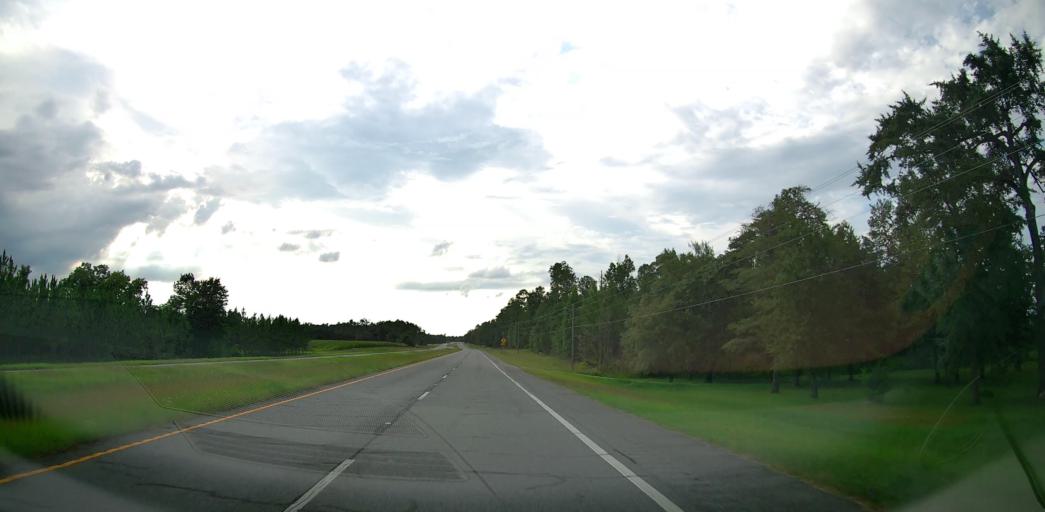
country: US
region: Georgia
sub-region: Pulaski County
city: Hawkinsville
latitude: 32.2687
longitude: -83.4136
